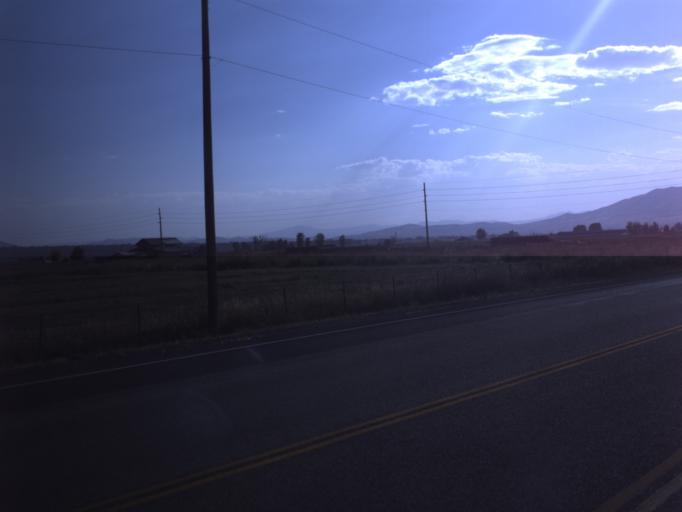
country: US
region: Utah
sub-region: Utah County
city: Salem
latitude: 40.0854
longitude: -111.6866
